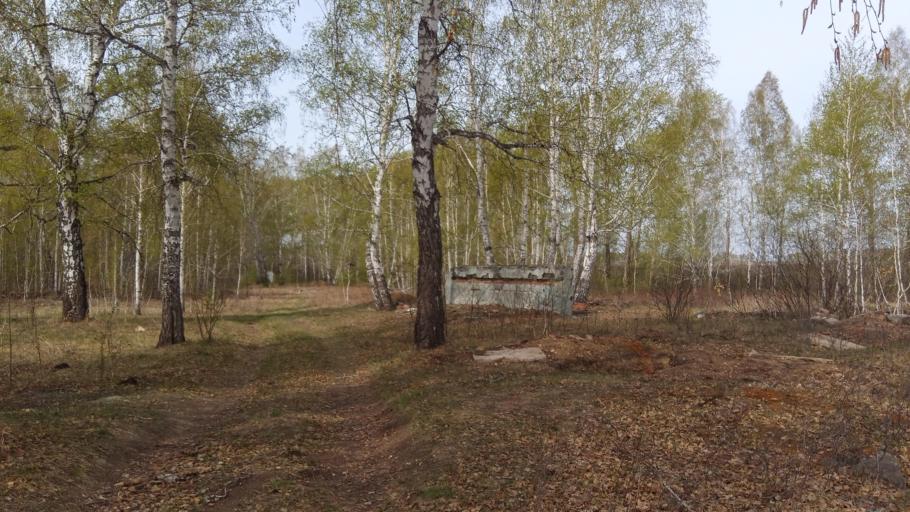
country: RU
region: Chelyabinsk
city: Timiryazevskiy
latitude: 55.0260
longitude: 60.8585
